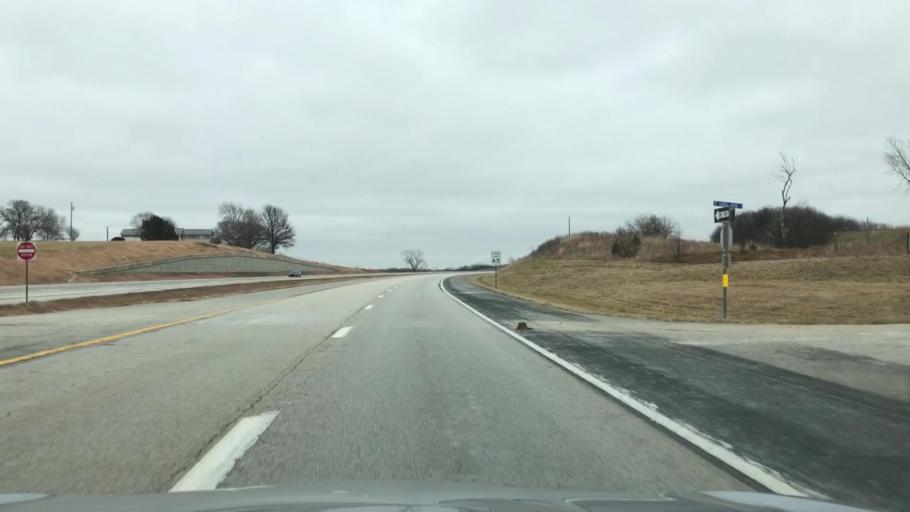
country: US
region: Missouri
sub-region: Caldwell County
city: Hamilton
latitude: 39.7488
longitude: -94.0560
